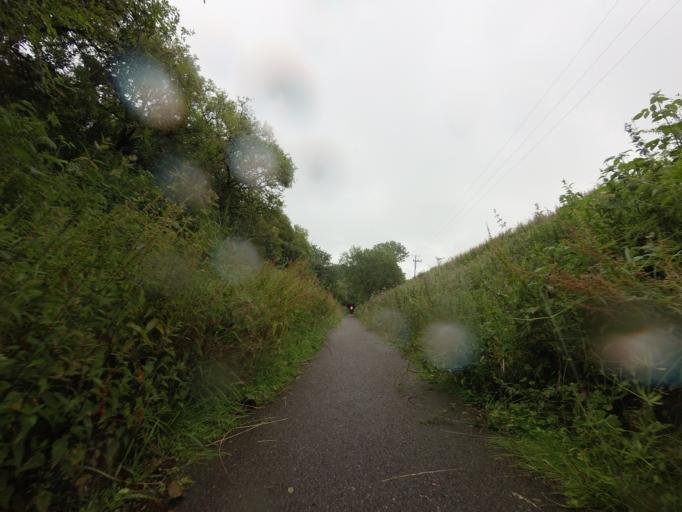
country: GB
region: Scotland
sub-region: Moray
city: Fochabers
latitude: 57.6626
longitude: -3.1087
